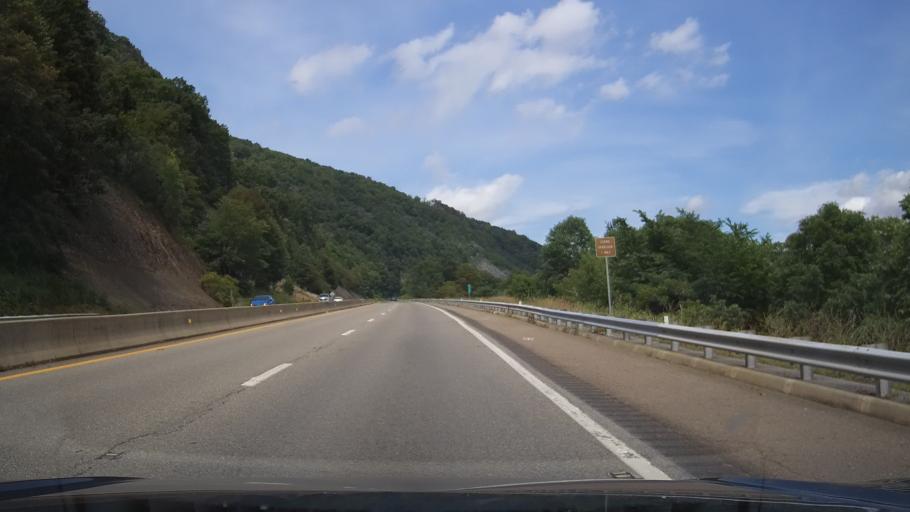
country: US
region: Virginia
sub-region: City of Norton
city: Norton
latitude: 36.9060
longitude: -82.6863
